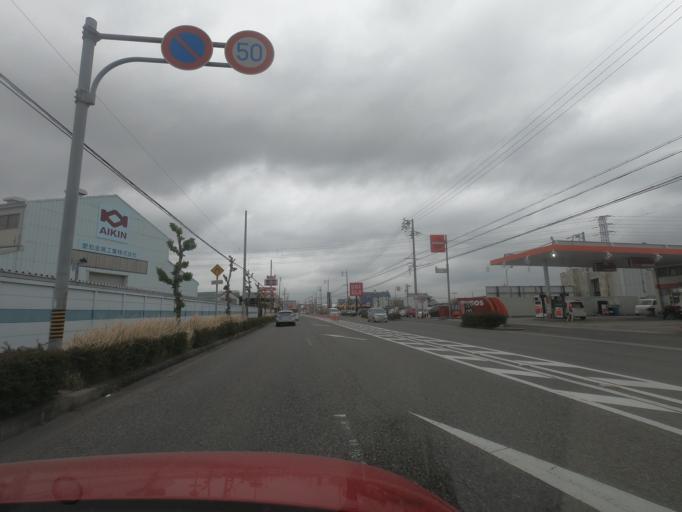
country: JP
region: Aichi
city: Kasugai
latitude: 35.2616
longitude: 136.9660
